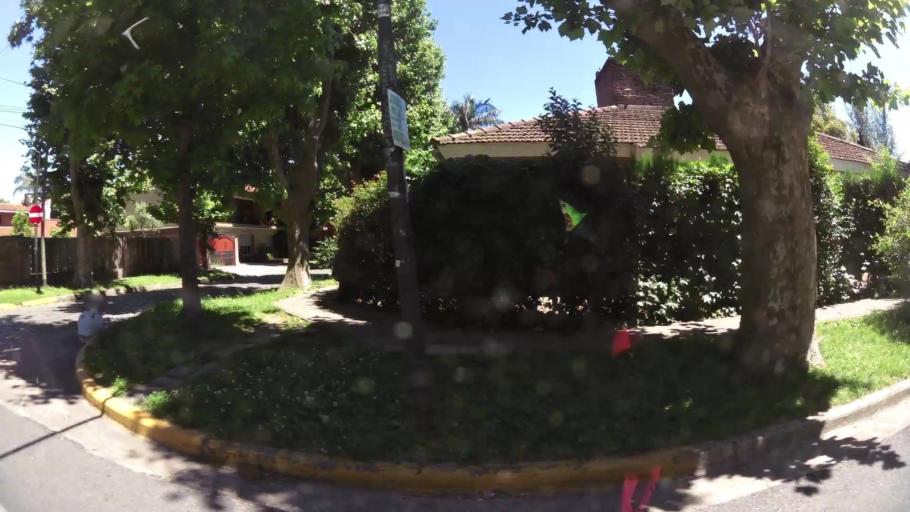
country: AR
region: Buenos Aires
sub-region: Partido de San Isidro
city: San Isidro
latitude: -34.5141
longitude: -58.5440
